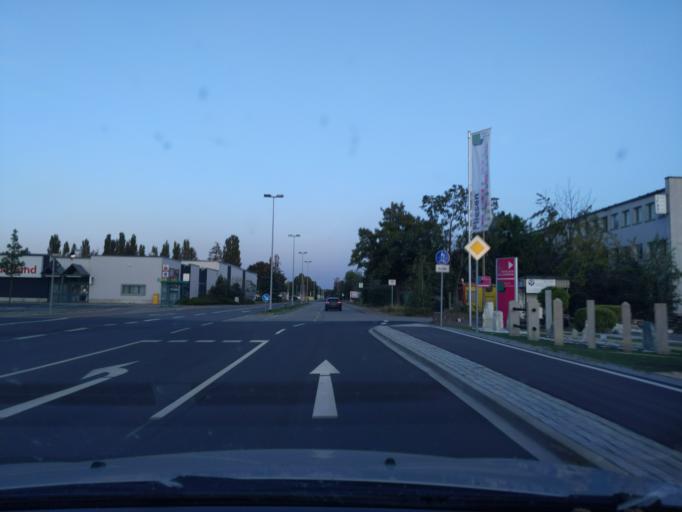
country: DE
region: Saxony
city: Hoyerswerda
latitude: 51.4310
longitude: 14.2847
